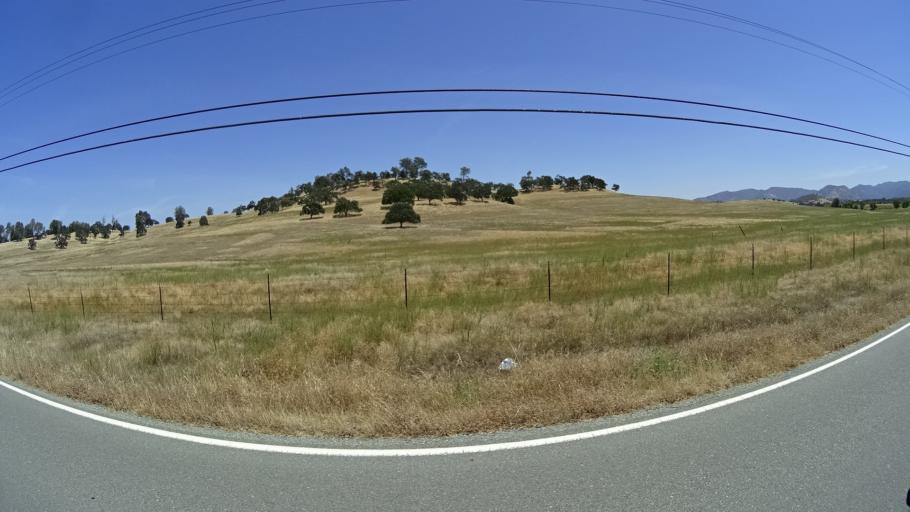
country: US
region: California
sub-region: Calaveras County
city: Valley Springs
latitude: 38.2218
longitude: -120.8352
